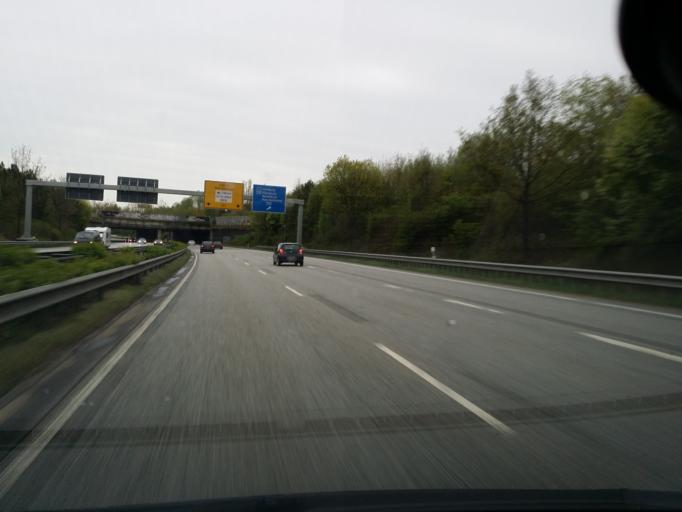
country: DE
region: Schleswig-Holstein
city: Kronshagen
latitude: 54.3215
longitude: 10.0978
